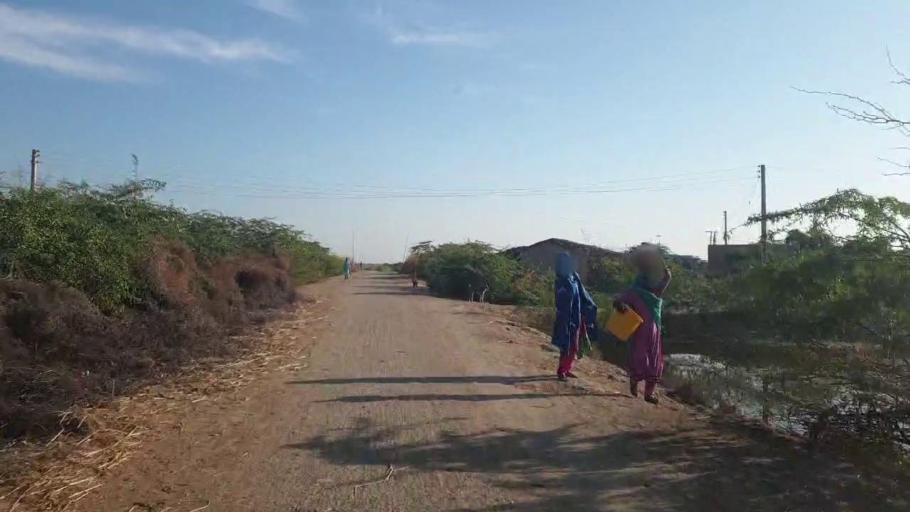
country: PK
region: Sindh
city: Talhar
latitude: 24.8364
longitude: 68.8440
